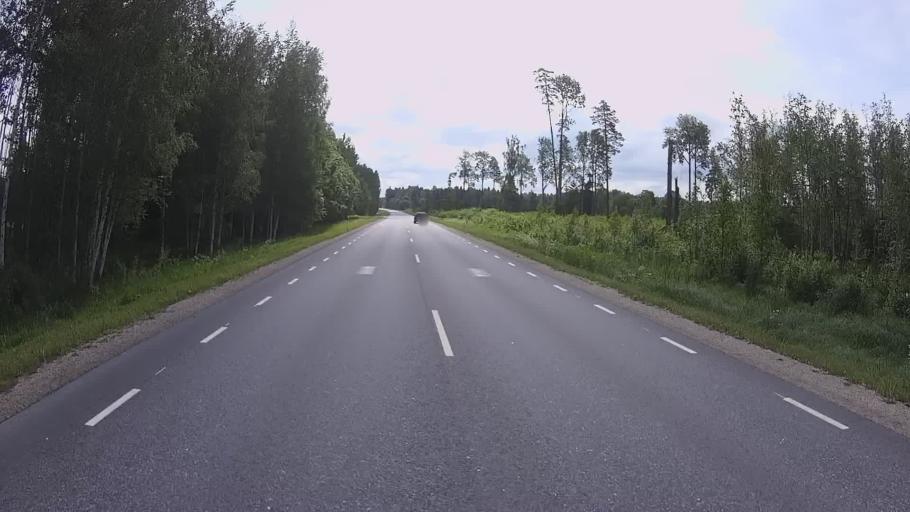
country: EE
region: Polvamaa
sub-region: Polva linn
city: Polva
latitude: 58.1697
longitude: 26.9124
